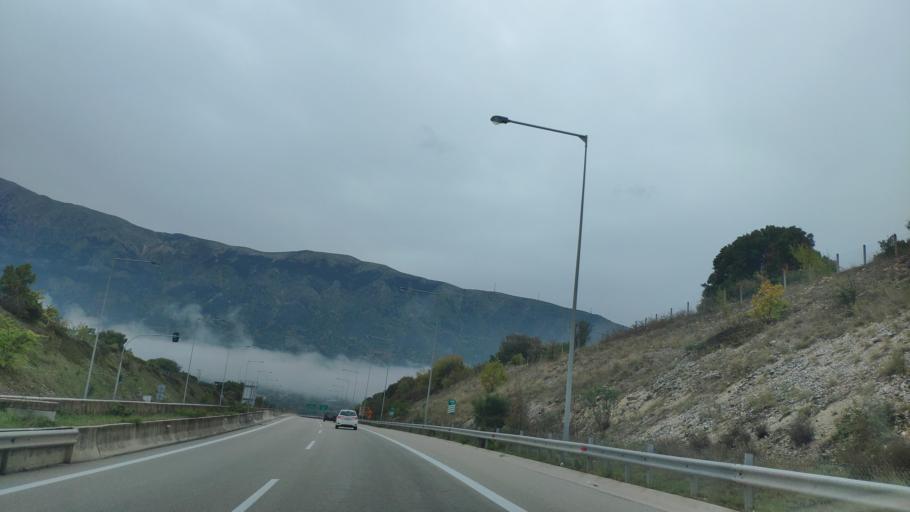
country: GR
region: Epirus
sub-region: Nomos Ioanninon
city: Pedini
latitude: 39.5666
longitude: 20.7804
